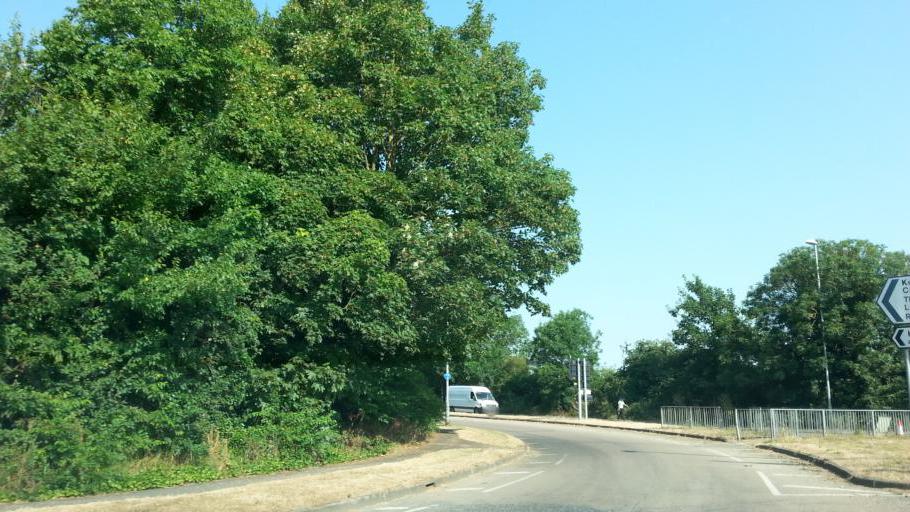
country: GB
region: England
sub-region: Cambridgeshire
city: Brampton
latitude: 52.3231
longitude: -0.2179
